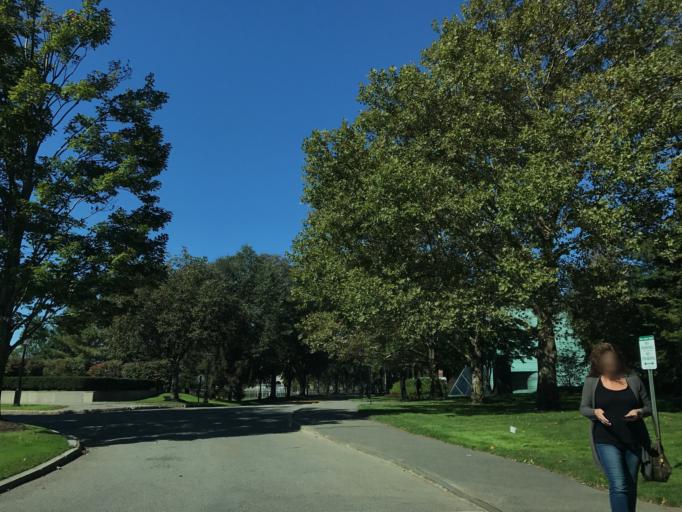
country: US
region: Massachusetts
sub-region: Middlesex County
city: Cambridge
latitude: 42.3654
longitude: -71.1231
